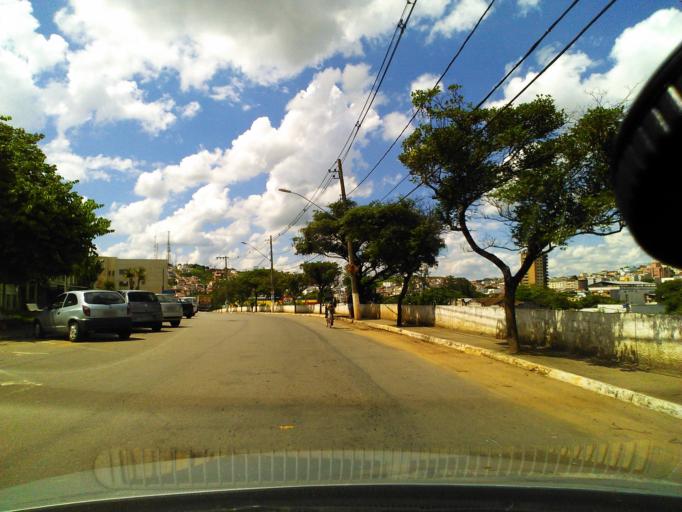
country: BR
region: Minas Gerais
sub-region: Tres Coracoes
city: Tres Coracoes
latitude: -21.7016
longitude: -45.2603
